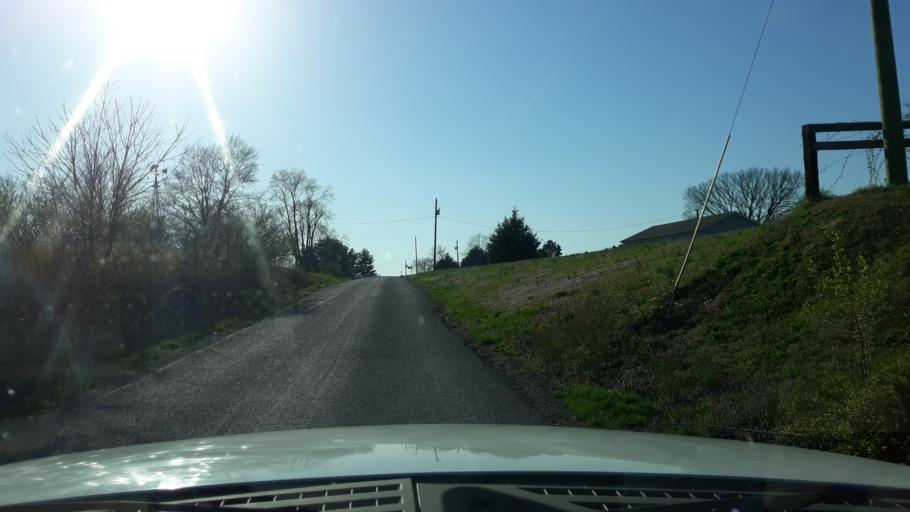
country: US
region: Illinois
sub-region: Saline County
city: Harrisburg
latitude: 37.7755
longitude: -88.5949
